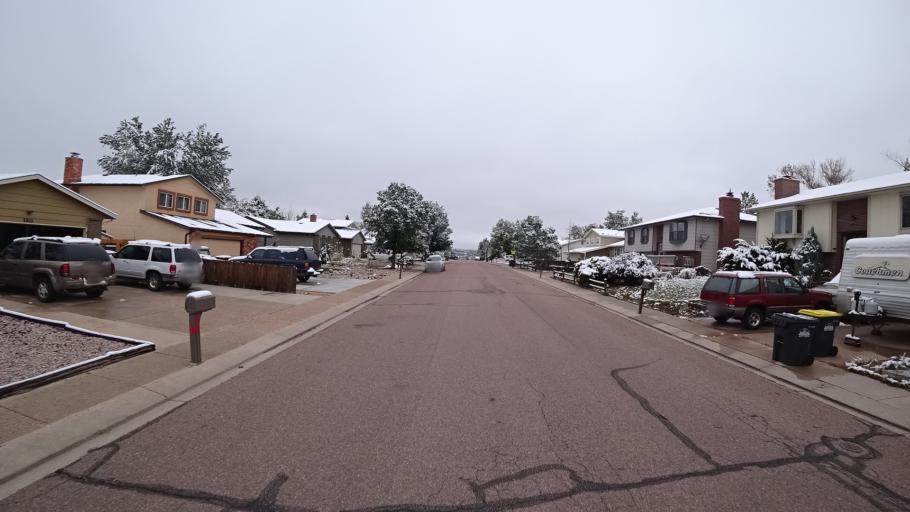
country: US
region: Colorado
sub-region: El Paso County
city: Colorado Springs
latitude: 38.9204
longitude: -104.7760
